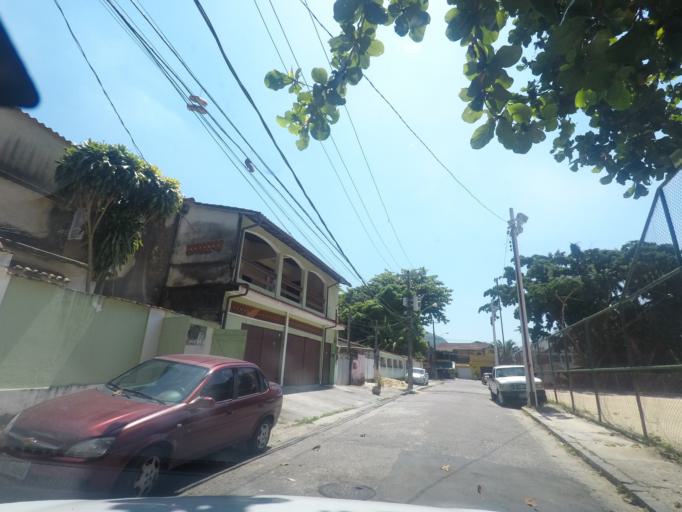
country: BR
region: Rio de Janeiro
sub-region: Nilopolis
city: Nilopolis
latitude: -22.9810
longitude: -43.4612
